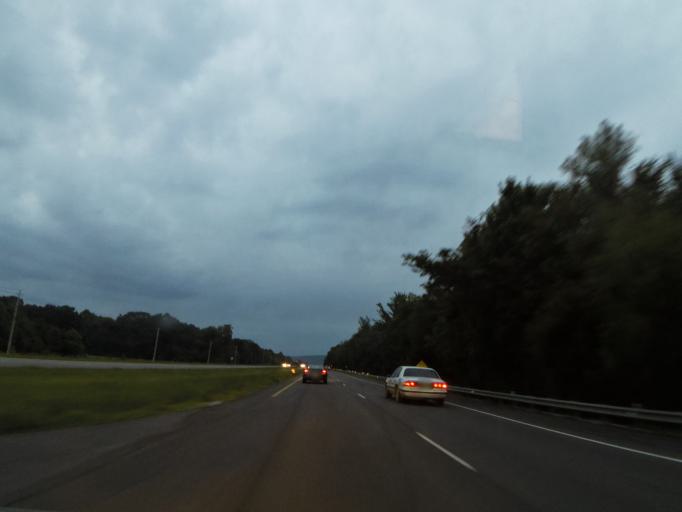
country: US
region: Alabama
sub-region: Madison County
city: Moores Mill
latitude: 34.7460
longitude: -86.4510
